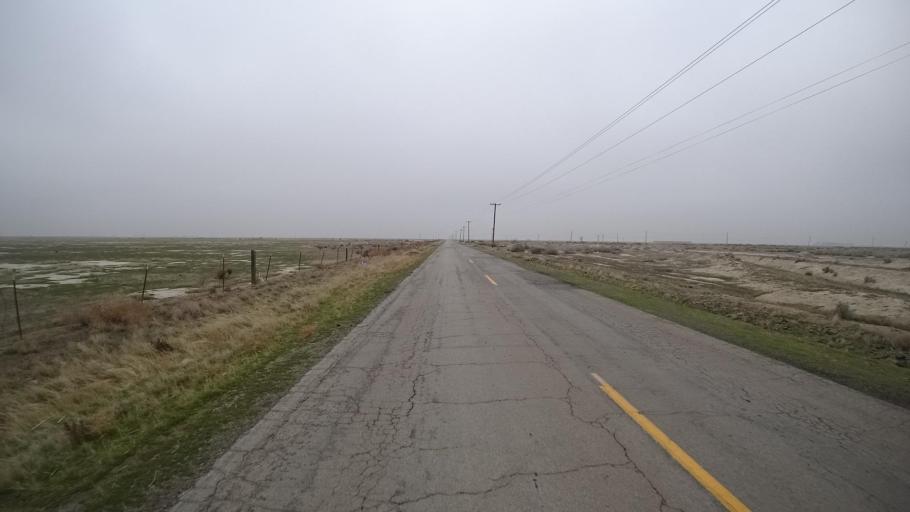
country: US
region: California
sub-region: Tulare County
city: Alpaugh
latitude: 35.7174
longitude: -119.4741
